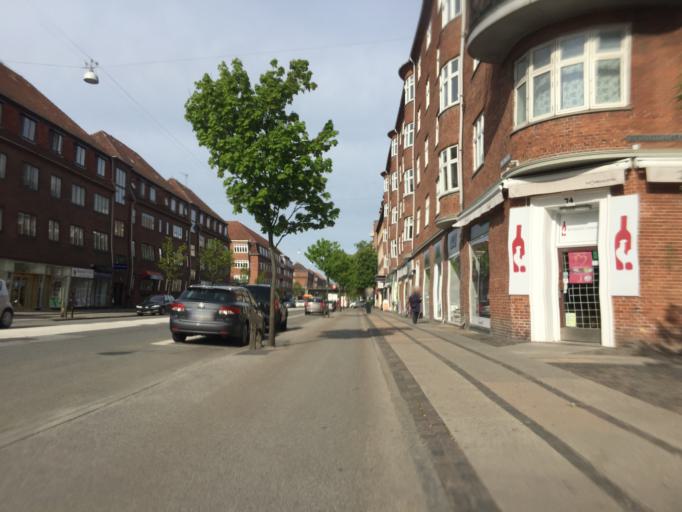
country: DK
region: Capital Region
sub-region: Kobenhavn
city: Vanlose
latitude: 55.6788
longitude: 12.5071
